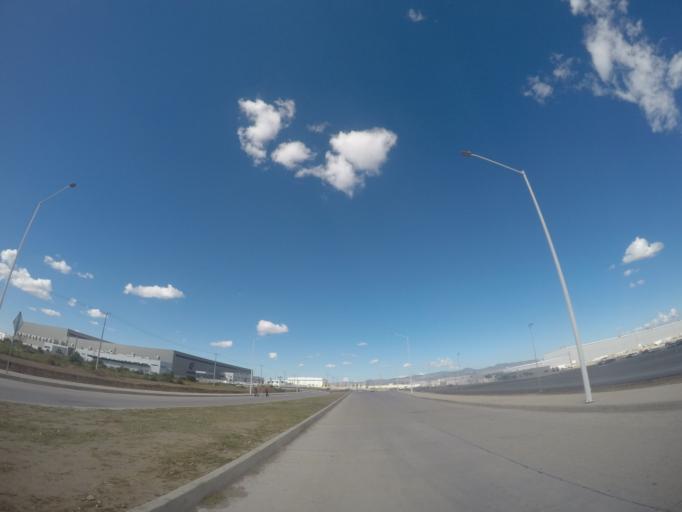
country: MX
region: San Luis Potosi
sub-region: Zaragoza
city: Cerro Gordo
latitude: 21.9715
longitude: -100.8566
